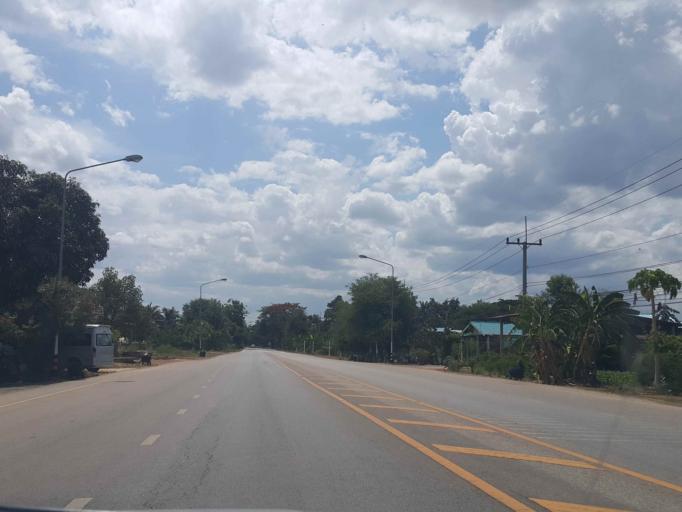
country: TH
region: Sukhothai
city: Thung Saliam
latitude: 17.3279
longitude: 99.6282
